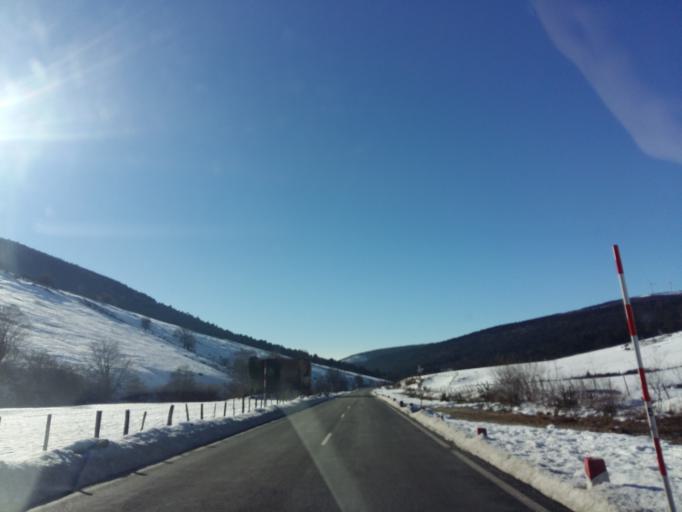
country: ES
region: Basque Country
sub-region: Bizkaia
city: Lanestosa
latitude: 43.1385
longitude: -3.4526
